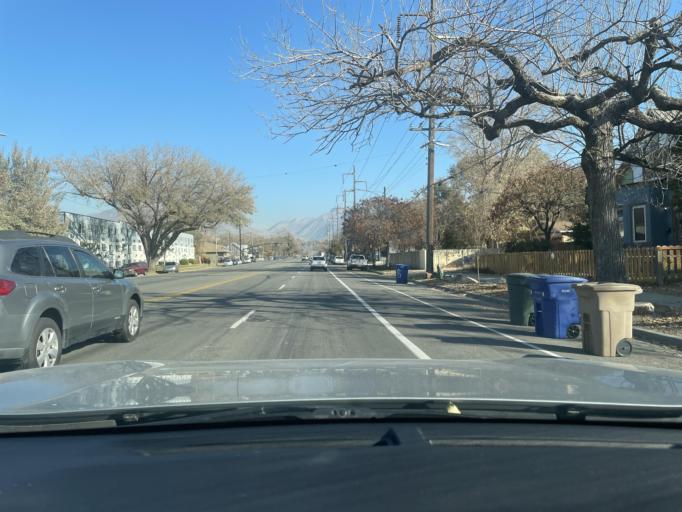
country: US
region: Utah
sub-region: Salt Lake County
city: Salt Lake City
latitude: 40.7519
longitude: -111.8821
